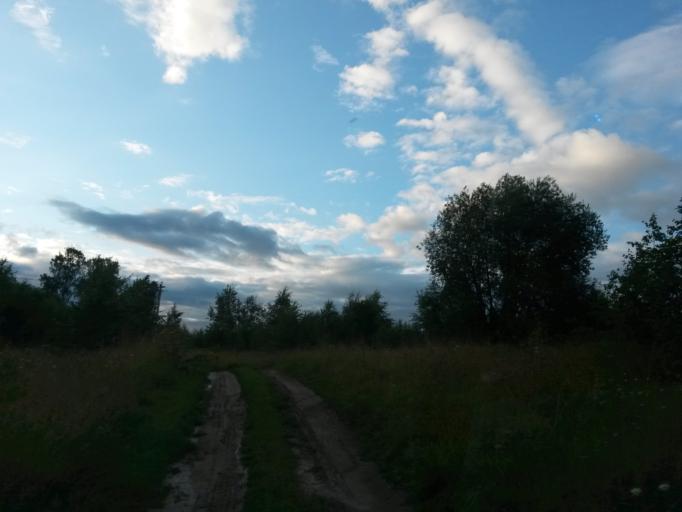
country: RU
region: Jaroslavl
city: Tutayev
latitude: 57.9360
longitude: 39.4462
